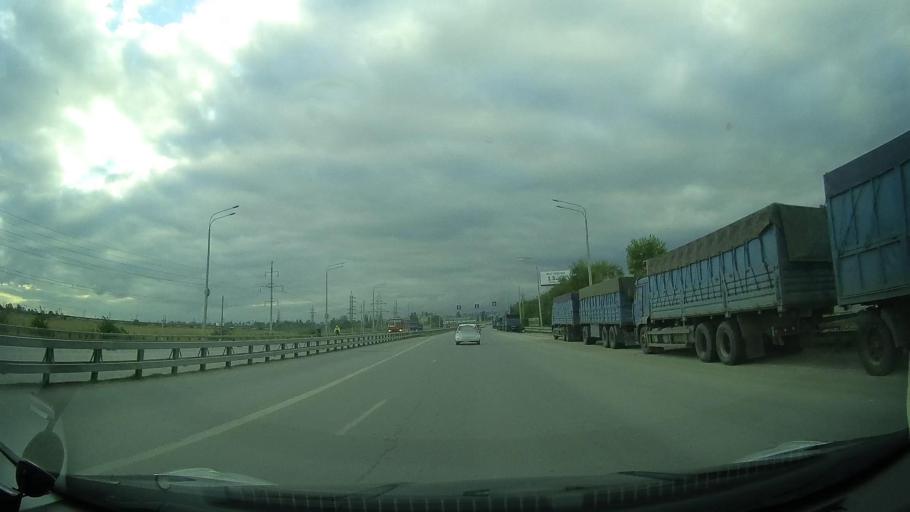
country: RU
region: Rostov
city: Rostov-na-Donu
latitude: 47.2023
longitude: 39.7195
